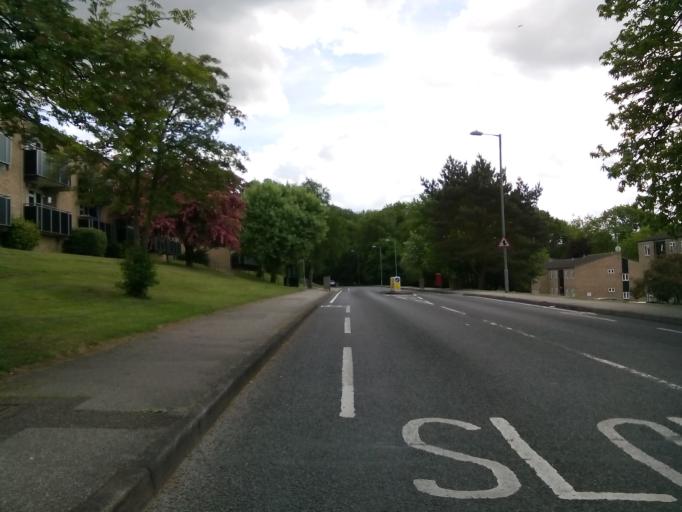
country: GB
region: England
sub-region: Suffolk
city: Ipswich
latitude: 52.0326
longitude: 1.1281
